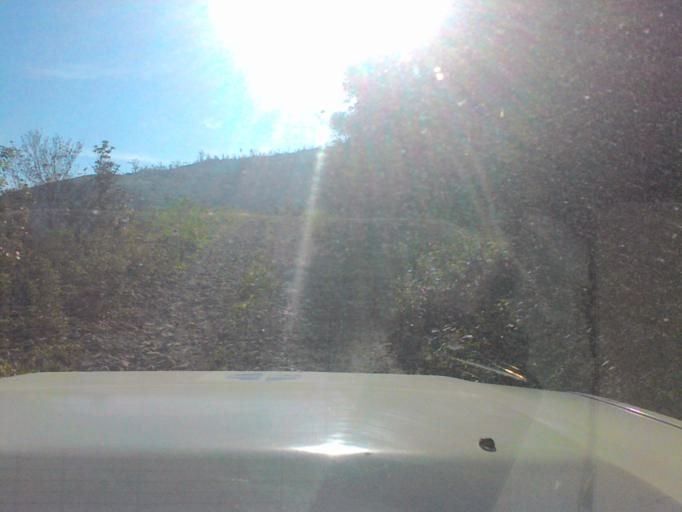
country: HT
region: Grandans
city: Jeremie
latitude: 18.5153
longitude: -74.0811
